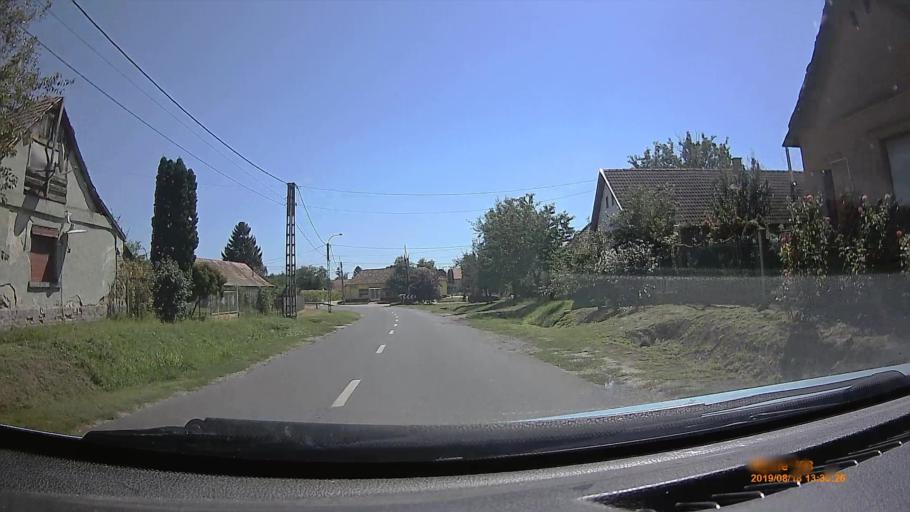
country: HU
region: Fejer
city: Cece
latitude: 46.7817
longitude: 18.5923
